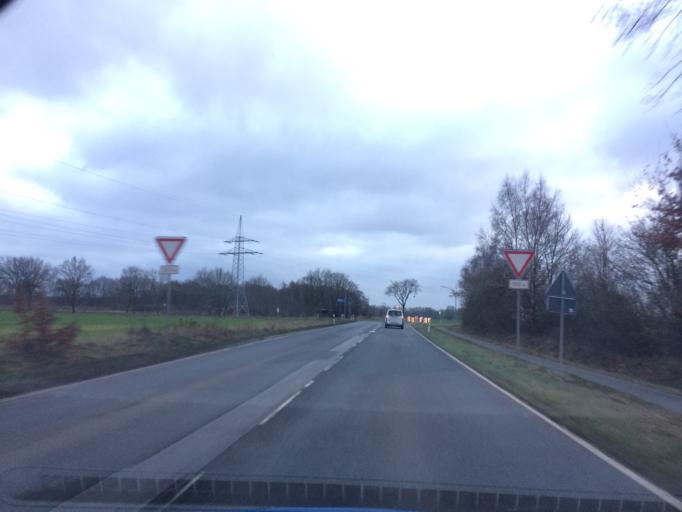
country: DE
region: Lower Saxony
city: Winsen
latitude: 53.3283
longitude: 10.2147
